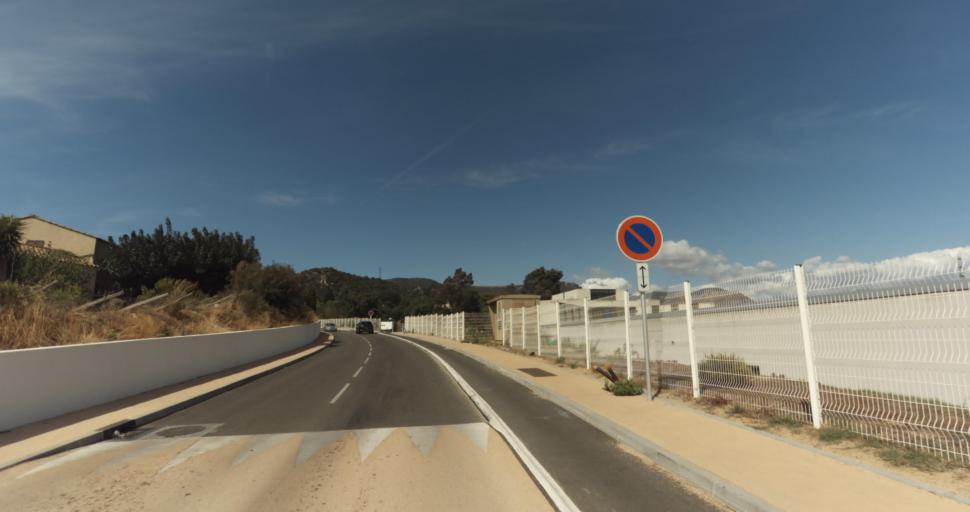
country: FR
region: Corsica
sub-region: Departement de la Corse-du-Sud
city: Ajaccio
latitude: 41.9467
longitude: 8.7582
